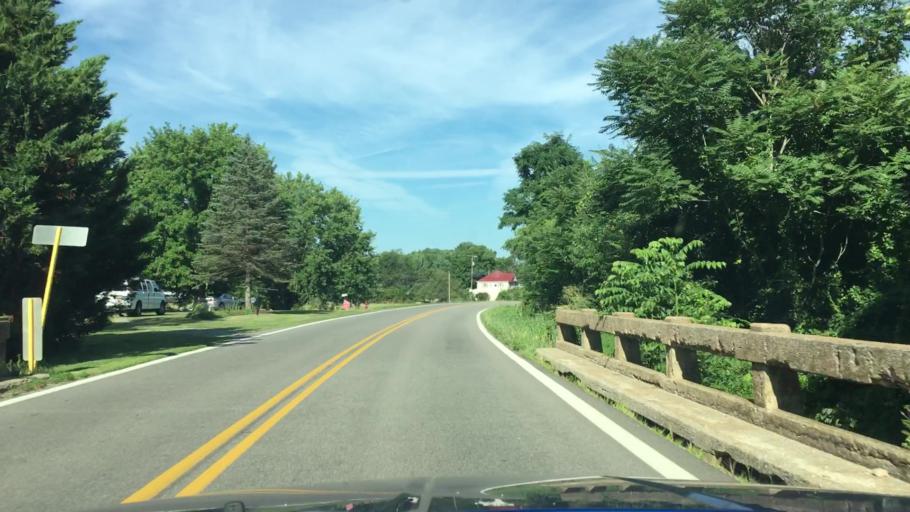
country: US
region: Virginia
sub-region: Augusta County
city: Lyndhurst
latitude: 38.0287
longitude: -78.9325
